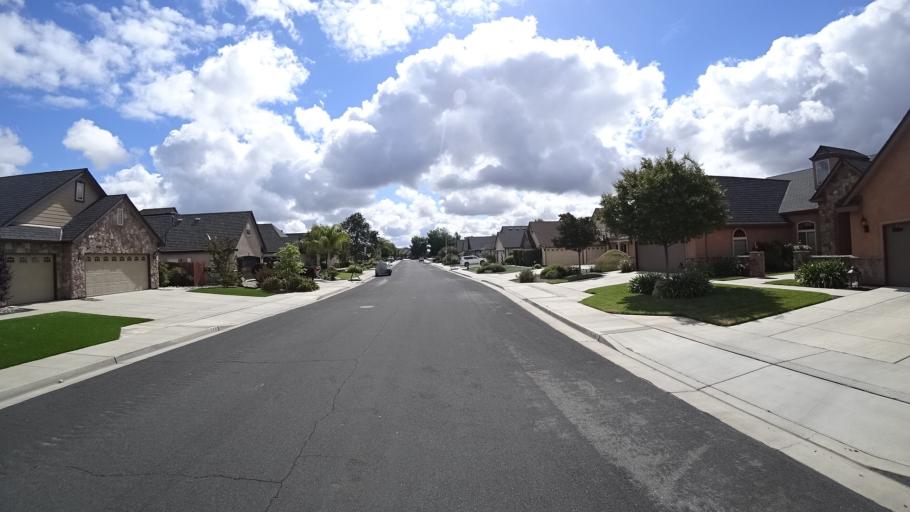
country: US
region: California
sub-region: Kings County
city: Lucerne
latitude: 36.3713
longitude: -119.6491
